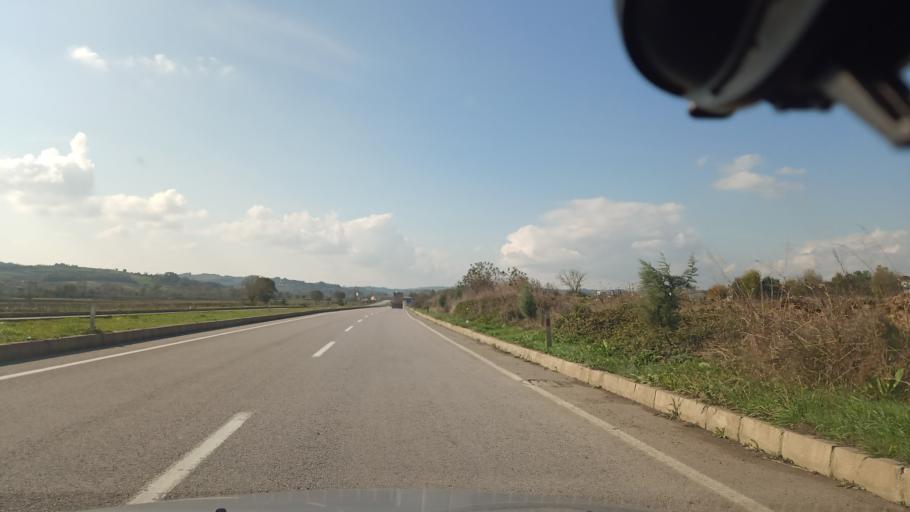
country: TR
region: Sakarya
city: Kaynarca
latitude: 41.0276
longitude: 30.3200
